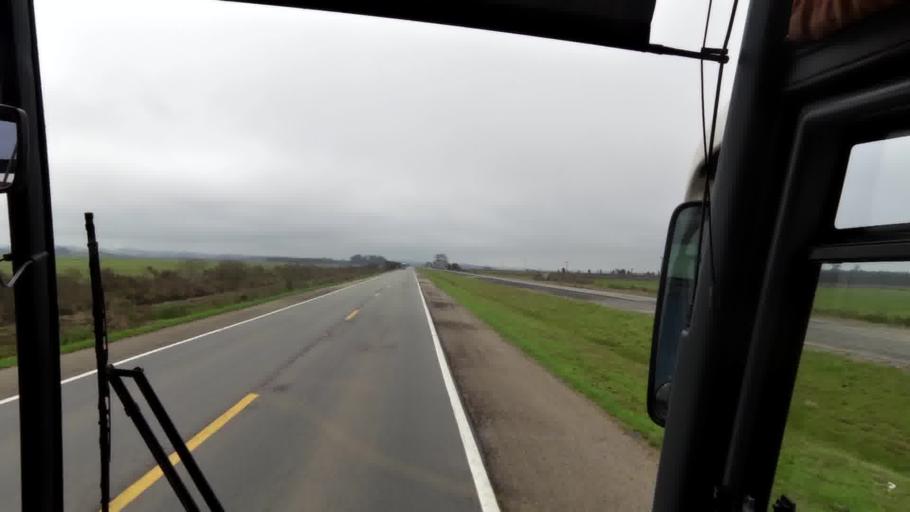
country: BR
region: Rio Grande do Sul
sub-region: Pelotas
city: Pelotas
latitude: -31.5946
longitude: -52.2863
